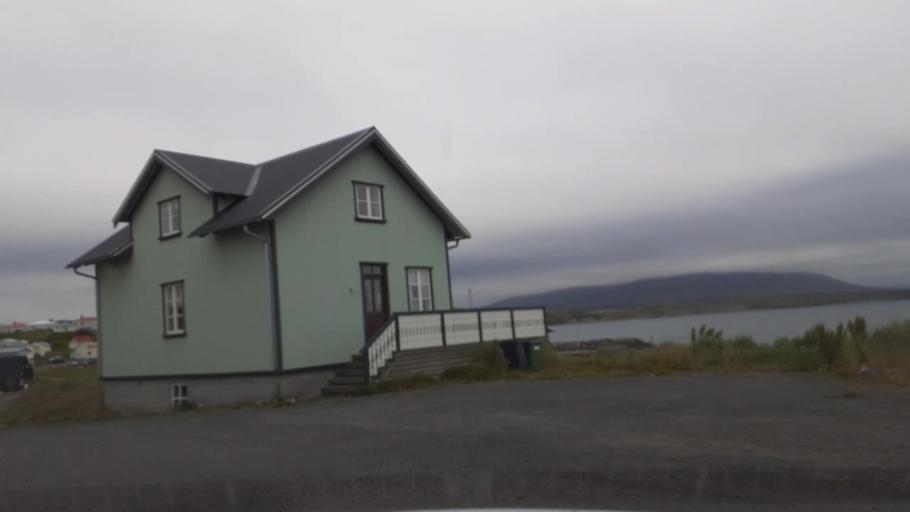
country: IS
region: Northwest
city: Saudarkrokur
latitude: 65.8990
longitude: -19.4230
